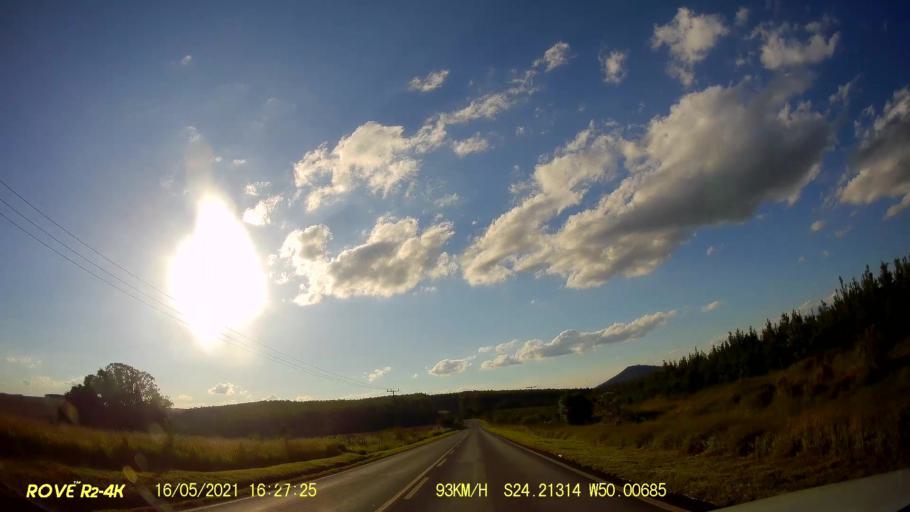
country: BR
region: Parana
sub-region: Jaguariaiva
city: Jaguariaiva
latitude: -24.2128
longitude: -50.0072
